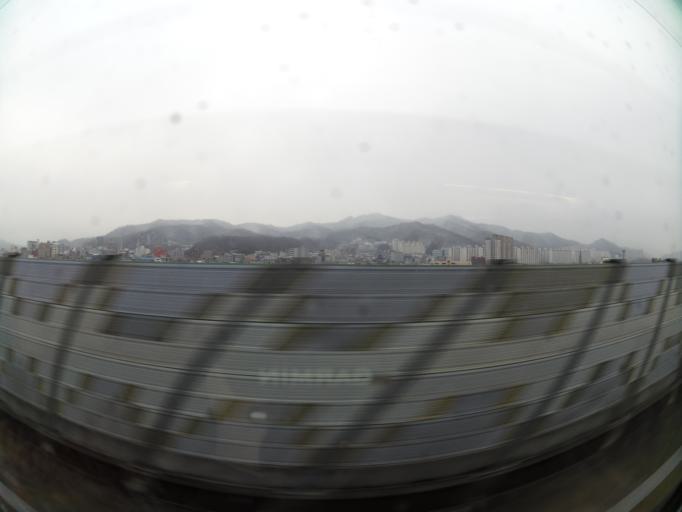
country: KR
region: Gyeongsangbuk-do
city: Gimcheon
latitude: 36.1303
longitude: 128.1068
